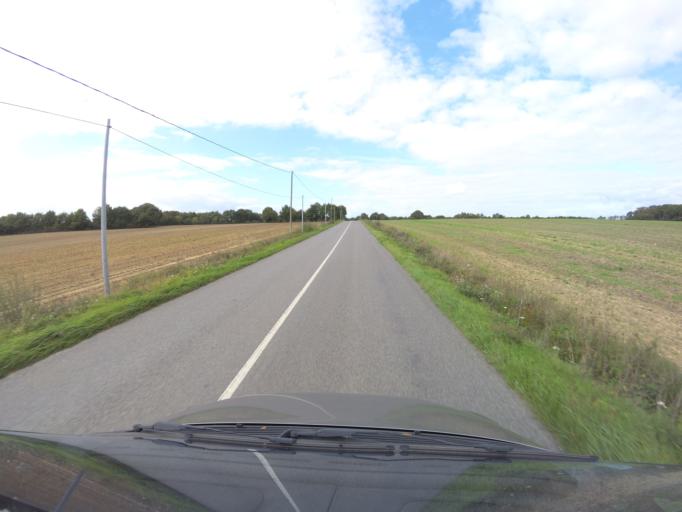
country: FR
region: Pays de la Loire
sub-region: Departement de la Loire-Atlantique
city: Bouvron
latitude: 47.4816
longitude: -1.8444
